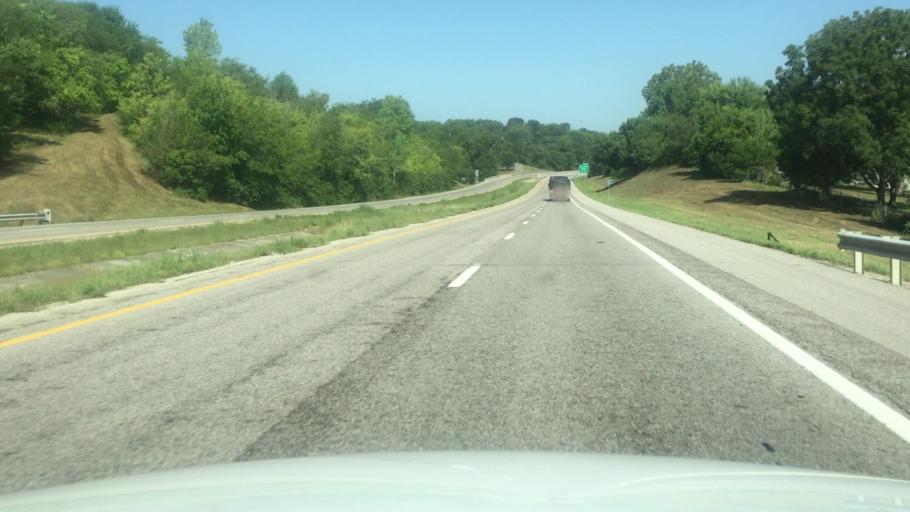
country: US
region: Missouri
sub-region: Buchanan County
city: Saint Joseph
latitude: 39.7252
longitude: -94.8396
